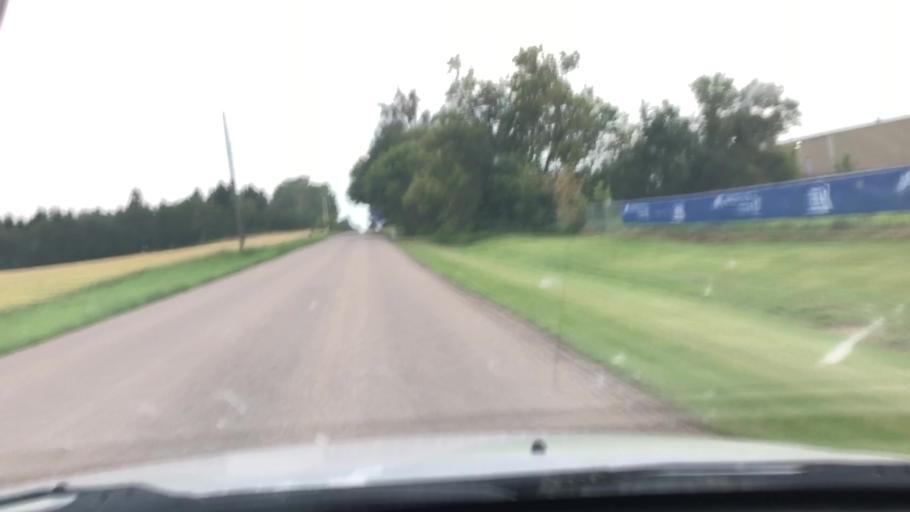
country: CA
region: Alberta
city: Devon
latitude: 53.4200
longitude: -113.6892
